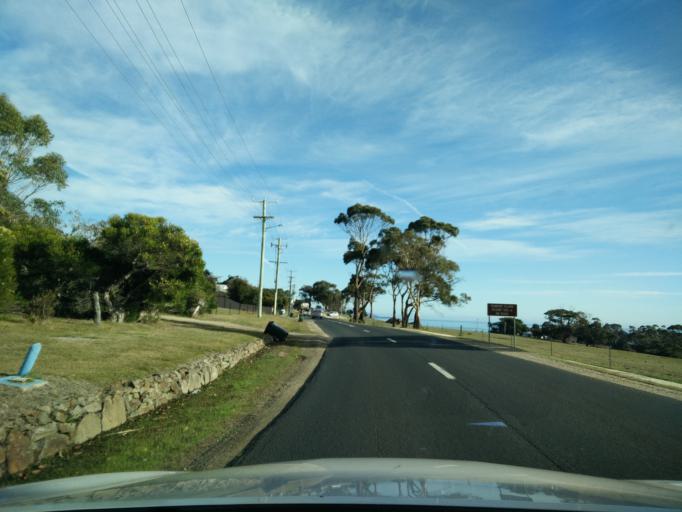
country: AU
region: Tasmania
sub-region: Break O'Day
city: St Helens
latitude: -41.8663
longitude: 148.2829
